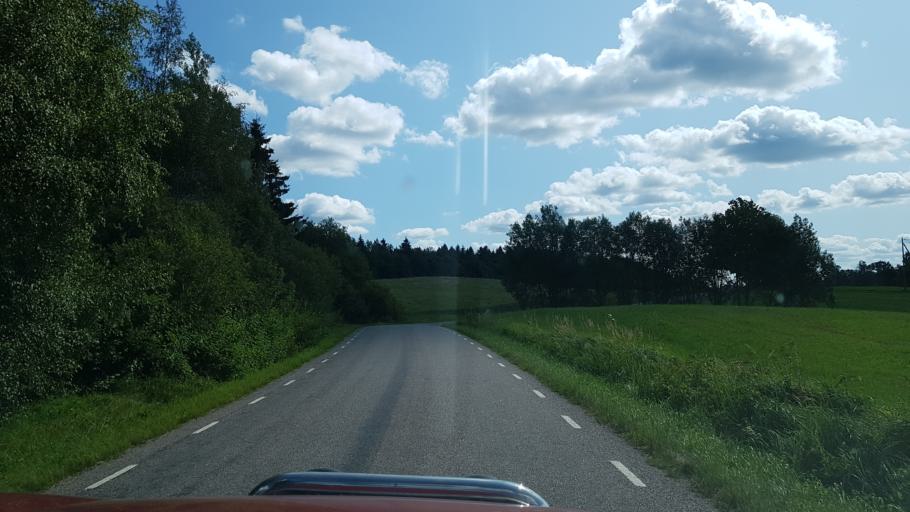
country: EE
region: Vorumaa
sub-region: Voru linn
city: Voru
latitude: 57.6442
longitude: 27.0869
